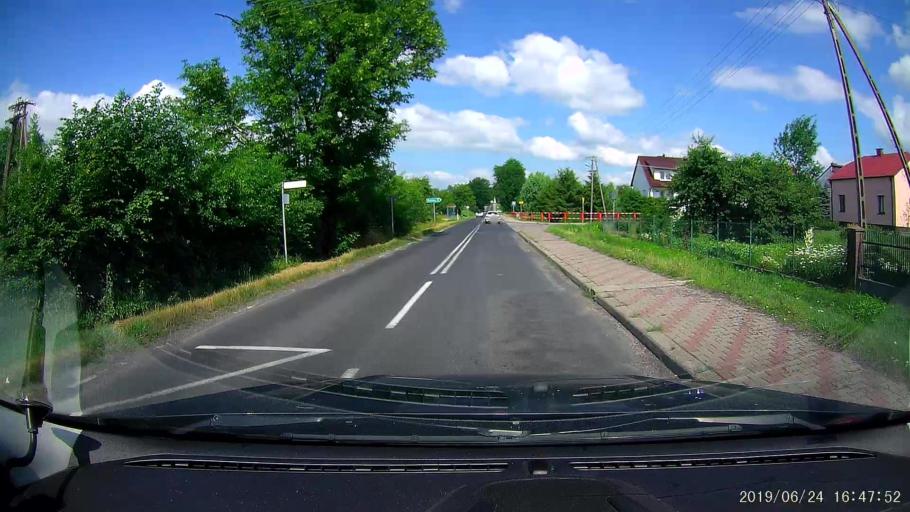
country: PL
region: Lublin Voivodeship
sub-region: Powiat tomaszowski
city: Laszczow
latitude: 50.5310
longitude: 23.7065
